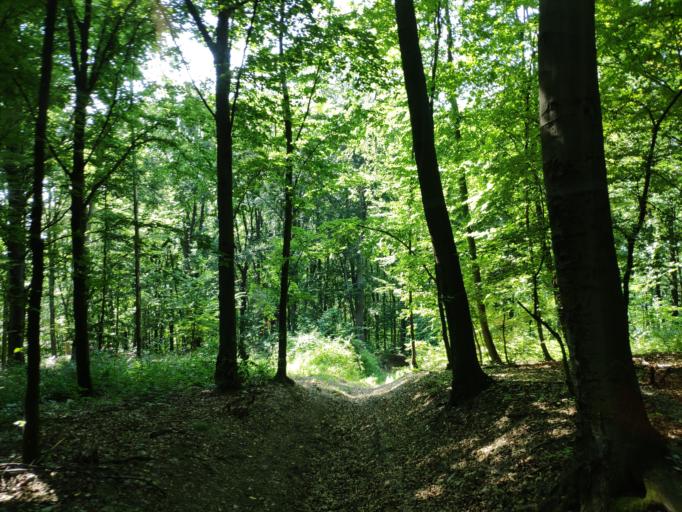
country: SK
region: Kosicky
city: Dobsina
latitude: 48.7087
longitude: 20.3755
